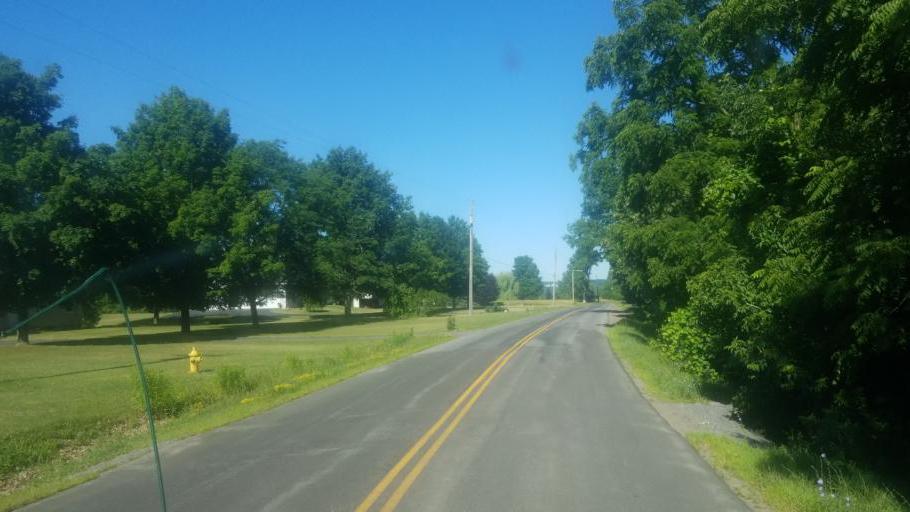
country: US
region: New York
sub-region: Ontario County
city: Canandaigua
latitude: 42.8391
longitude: -77.2376
